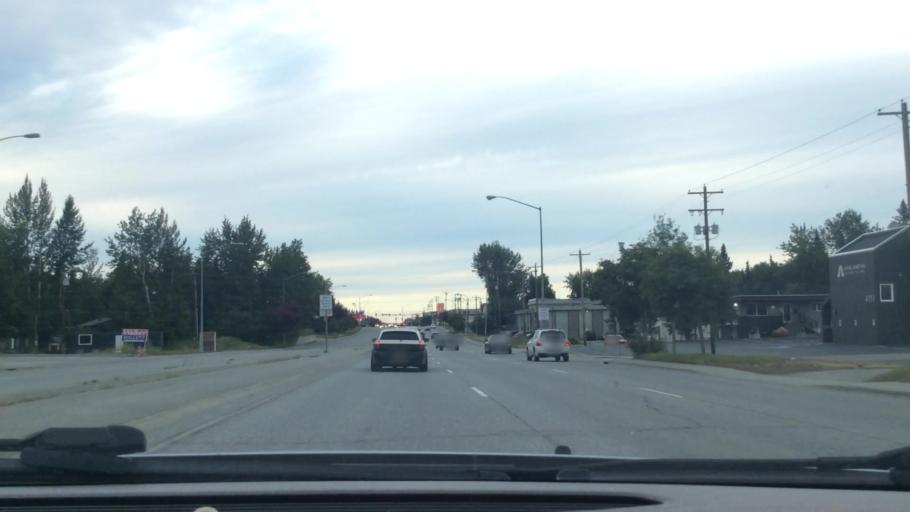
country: US
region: Alaska
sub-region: Anchorage Municipality
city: Anchorage
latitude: 61.1824
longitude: -149.9131
